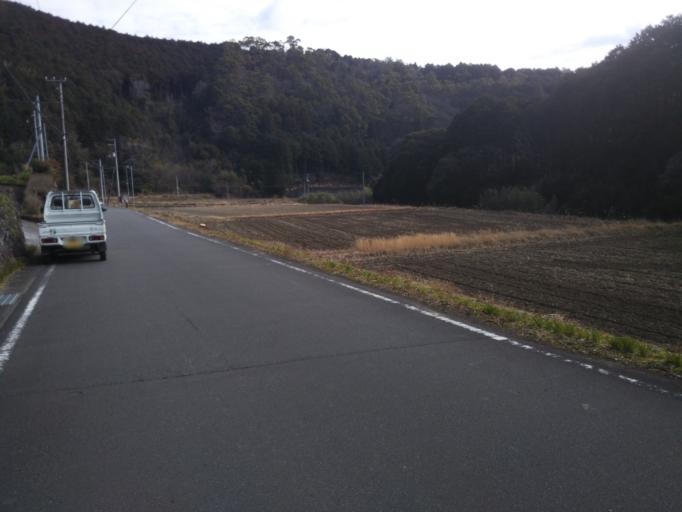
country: JP
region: Kochi
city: Nakamura
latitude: 33.0381
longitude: 132.9755
